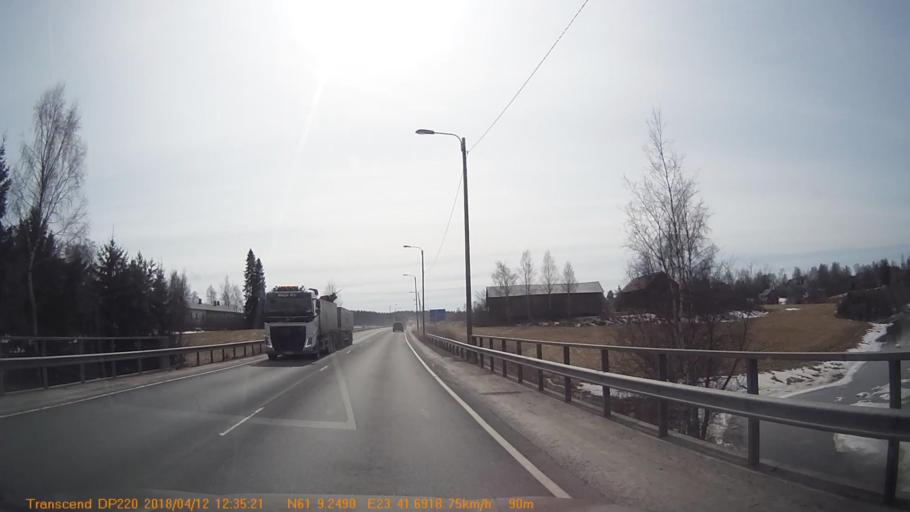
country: FI
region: Pirkanmaa
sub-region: Etelae-Pirkanmaa
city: Kylmaekoski
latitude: 61.1543
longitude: 23.6949
